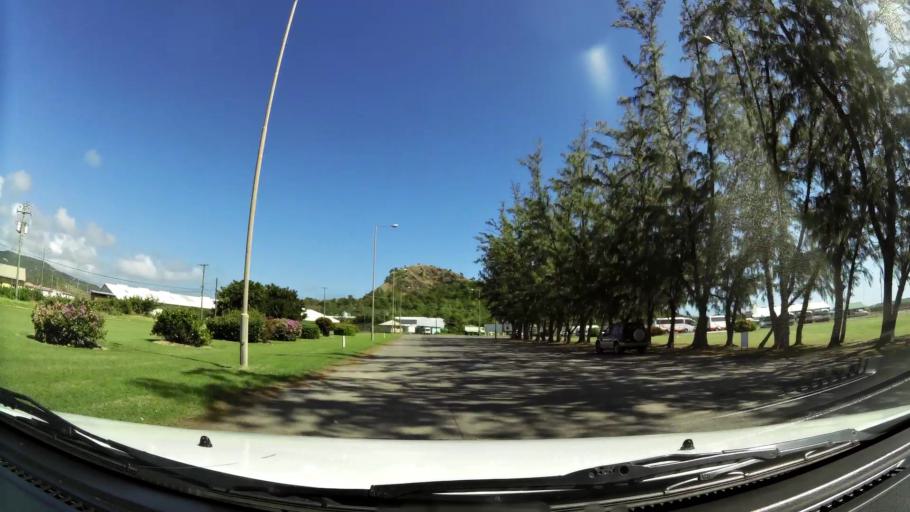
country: LC
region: Vieux-Fort
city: Vieux Fort
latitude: 13.7377
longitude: -60.9498
